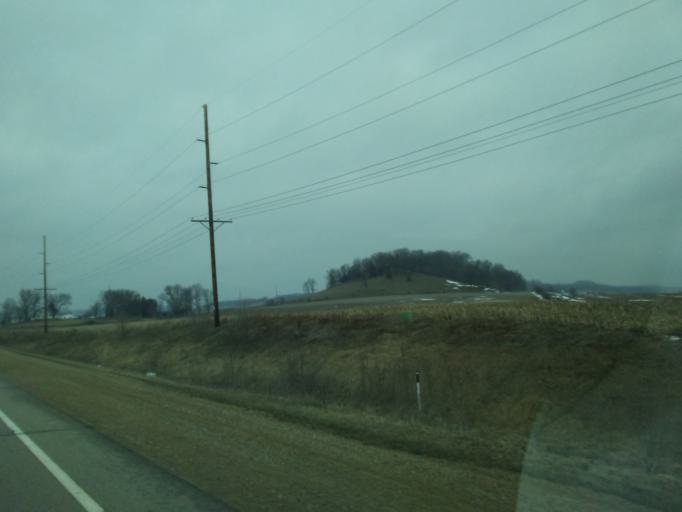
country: US
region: Wisconsin
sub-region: Richland County
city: Richland Center
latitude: 43.2887
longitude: -90.3182
